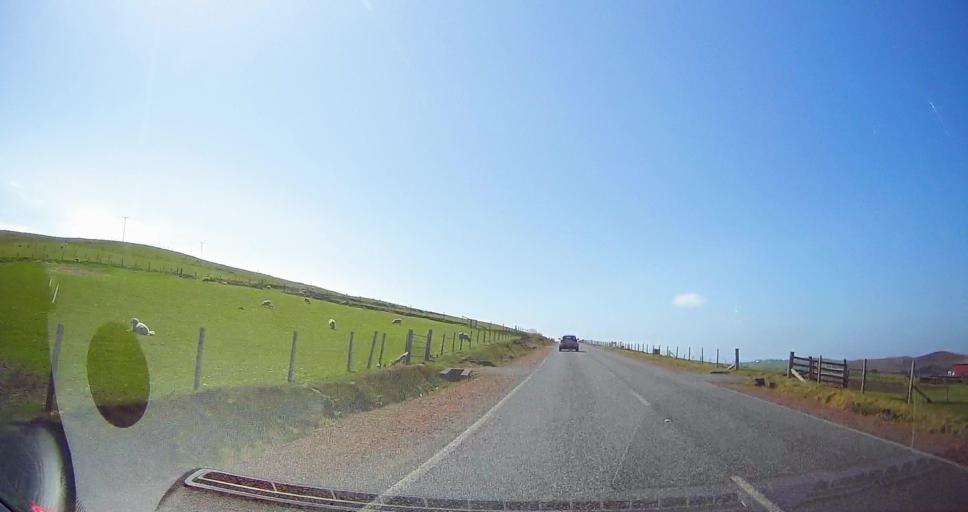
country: GB
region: Scotland
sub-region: Shetland Islands
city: Sandwick
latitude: 60.1163
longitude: -1.2929
